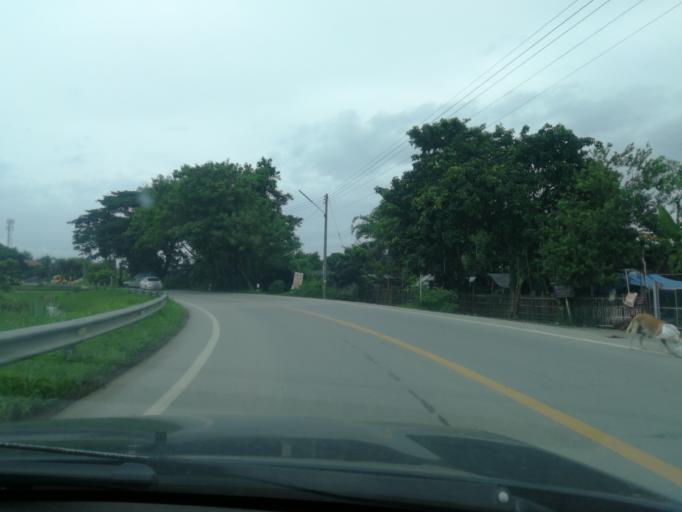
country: TH
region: Chiang Mai
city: San Pa Tong
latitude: 18.6292
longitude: 98.8992
